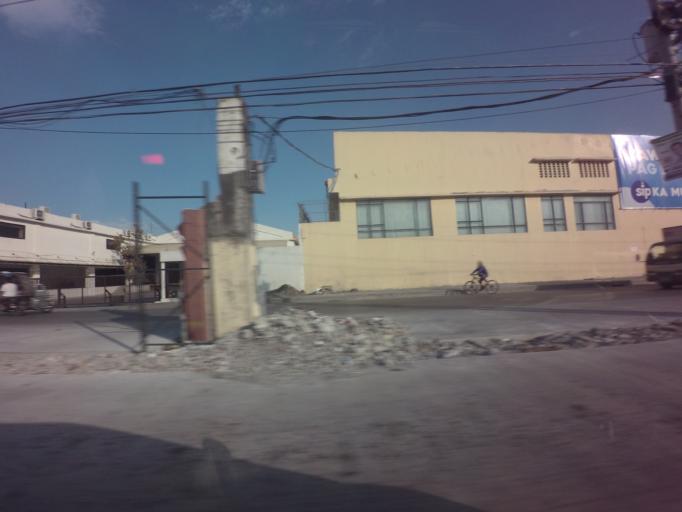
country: PH
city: Sambayanihan People's Village
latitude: 14.4993
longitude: 121.0060
